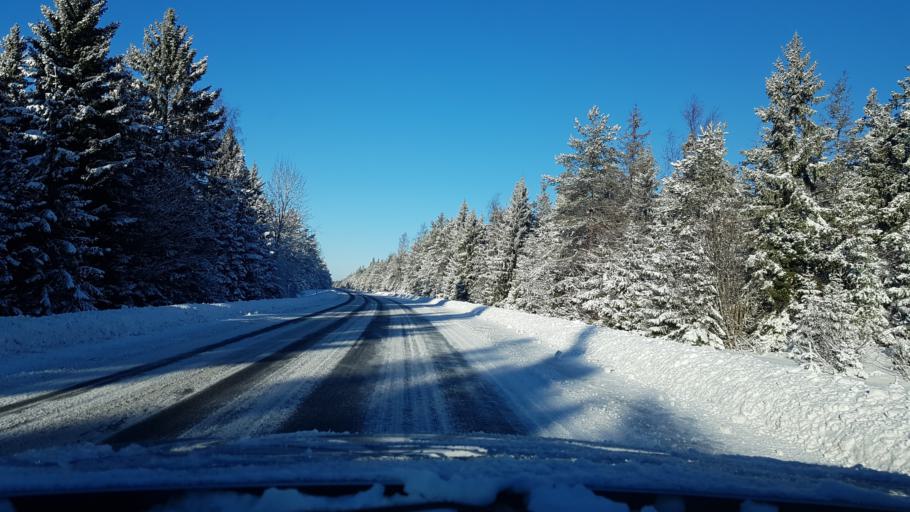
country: EE
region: Hiiumaa
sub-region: Kaerdla linn
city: Kardla
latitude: 58.9817
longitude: 22.8077
